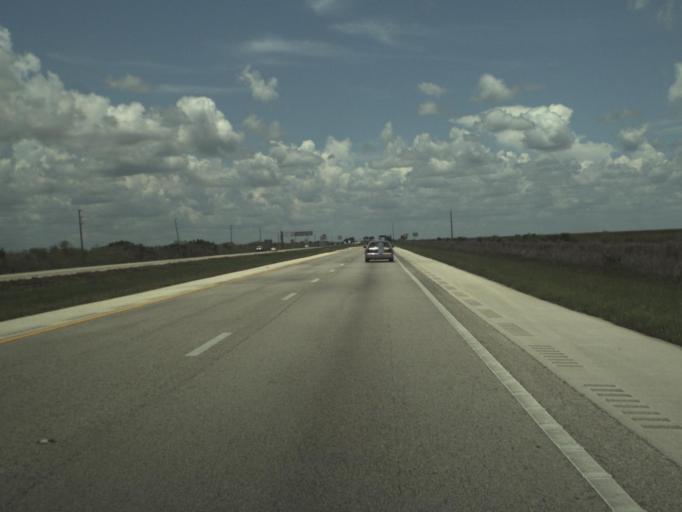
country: US
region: Florida
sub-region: Broward County
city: Weston
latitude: 26.1466
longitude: -80.6535
